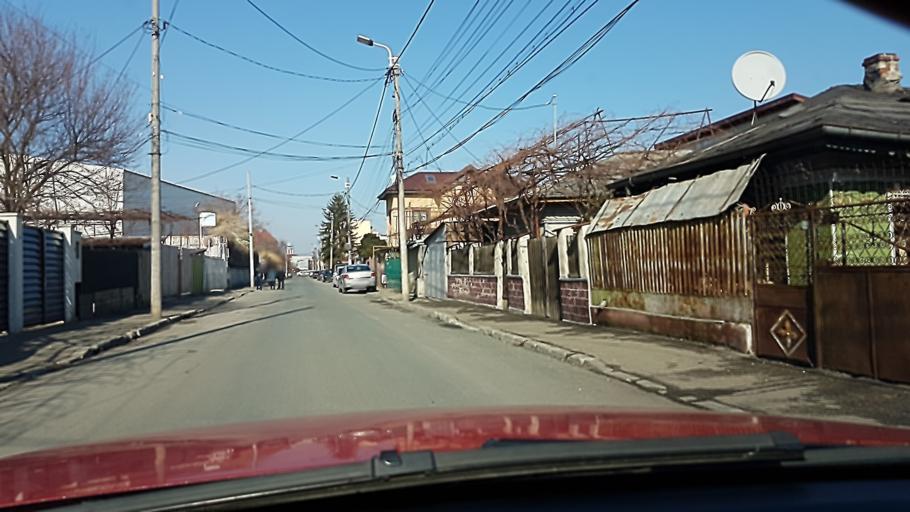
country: RO
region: Ilfov
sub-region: Comuna Pantelimon
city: Pantelimon
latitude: 44.4289
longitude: 26.1969
